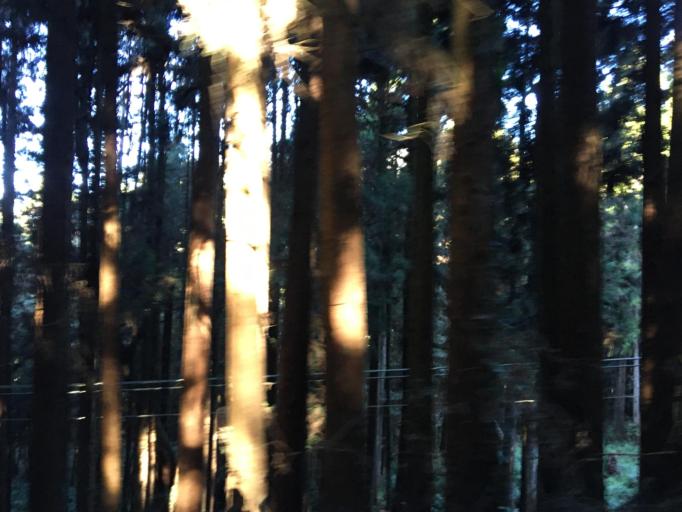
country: TW
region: Taiwan
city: Lugu
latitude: 23.5146
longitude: 120.8010
